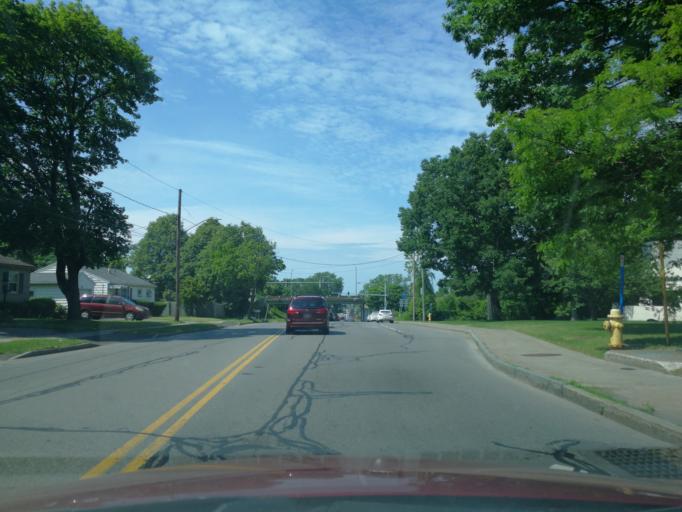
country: US
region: New York
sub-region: Monroe County
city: Irondequoit
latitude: 43.1920
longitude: -77.5921
